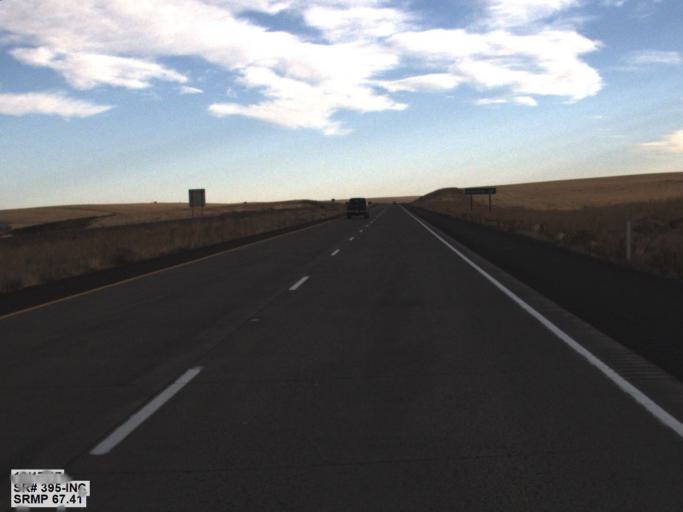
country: US
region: Washington
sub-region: Franklin County
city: Connell
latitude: 46.8011
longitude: -118.7320
